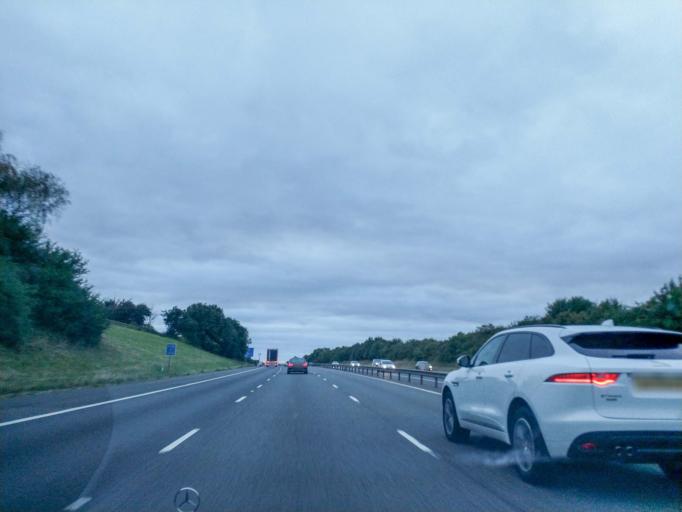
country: GB
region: England
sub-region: Warwickshire
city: Harbury
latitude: 52.2045
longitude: -1.4772
